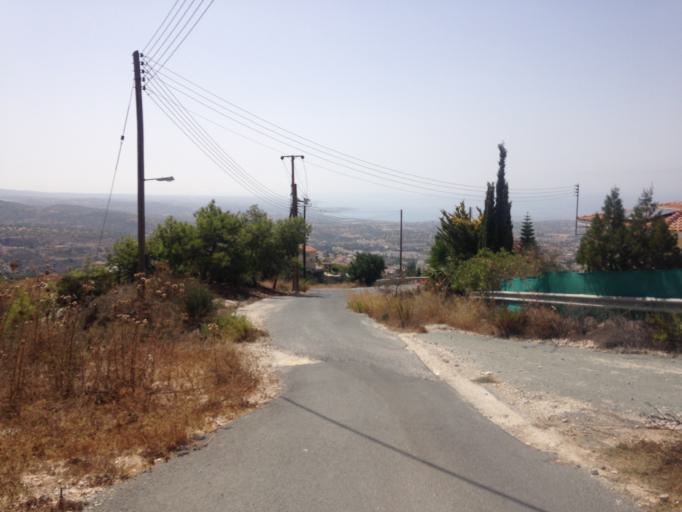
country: CY
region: Pafos
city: Pegeia
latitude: 34.8908
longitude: 32.3873
